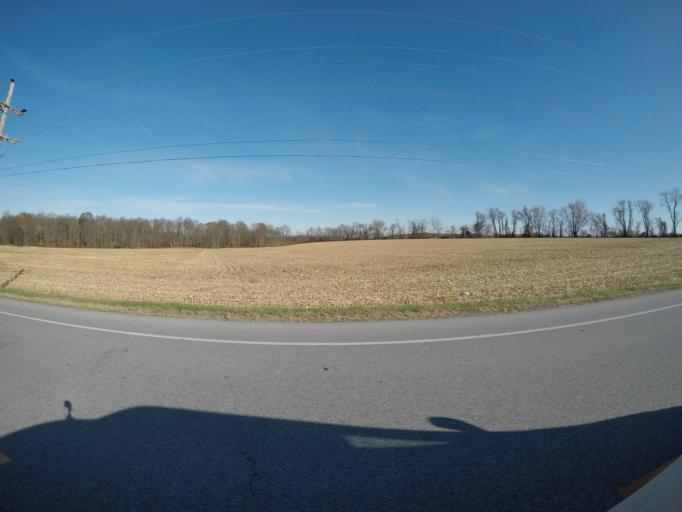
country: US
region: Pennsylvania
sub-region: Chester County
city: Parkesburg
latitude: 39.9257
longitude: -75.9161
